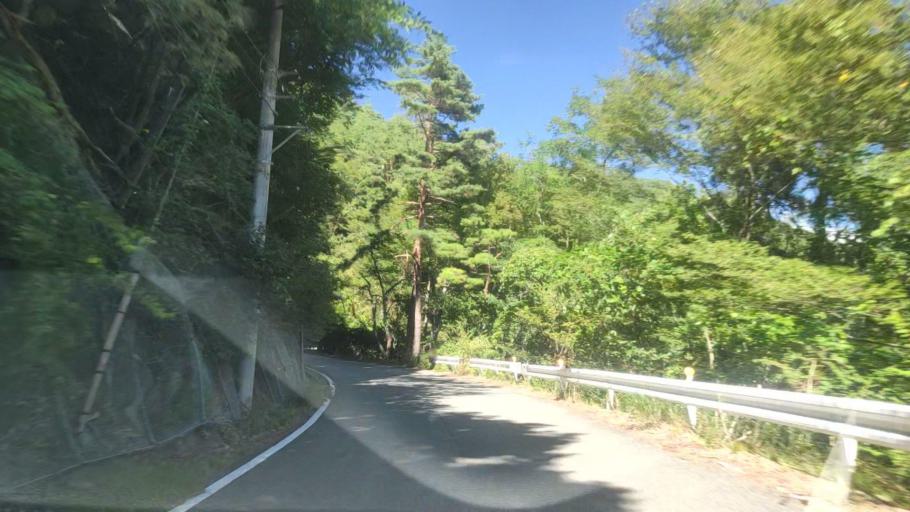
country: JP
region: Yamanashi
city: Fujikawaguchiko
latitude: 35.5461
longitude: 138.7734
